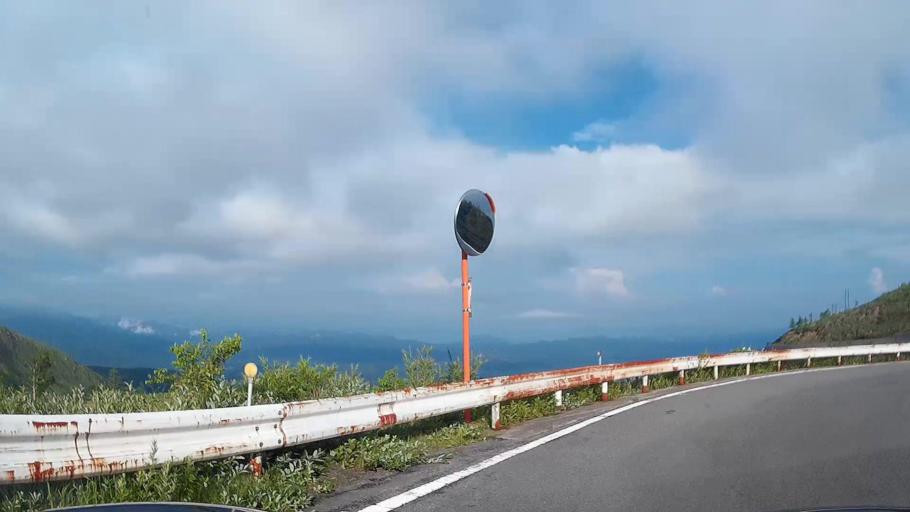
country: JP
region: Nagano
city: Nakano
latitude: 36.6363
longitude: 138.5459
